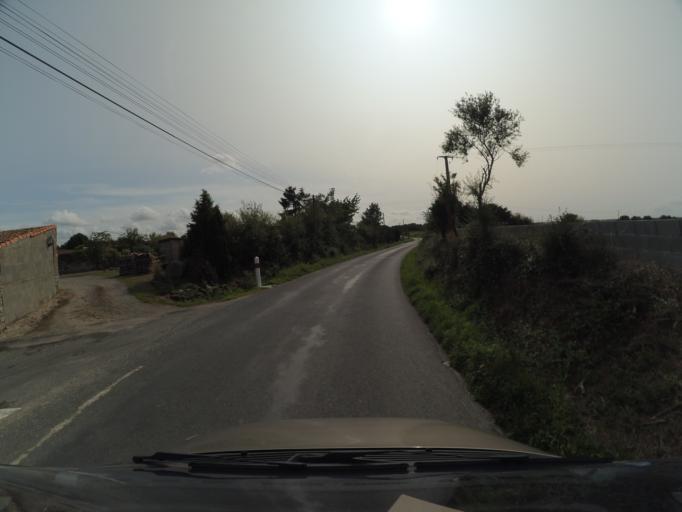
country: FR
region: Pays de la Loire
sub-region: Departement de la Loire-Atlantique
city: Boussay
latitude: 47.0186
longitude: -1.1632
